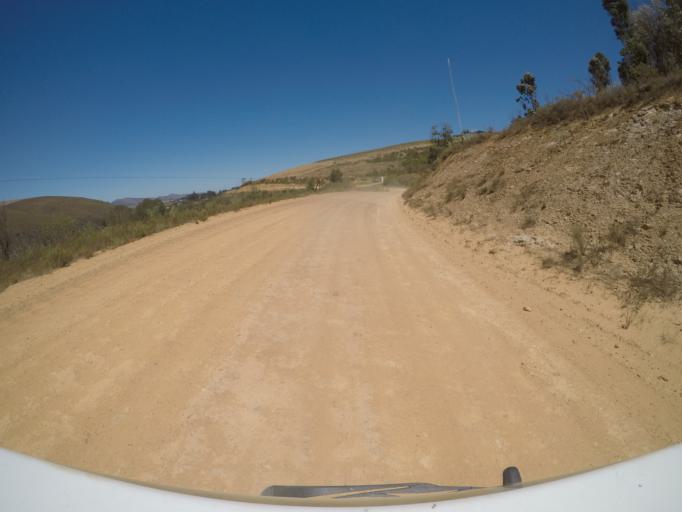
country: ZA
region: Western Cape
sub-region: Overberg District Municipality
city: Grabouw
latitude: -34.2134
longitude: 19.2105
